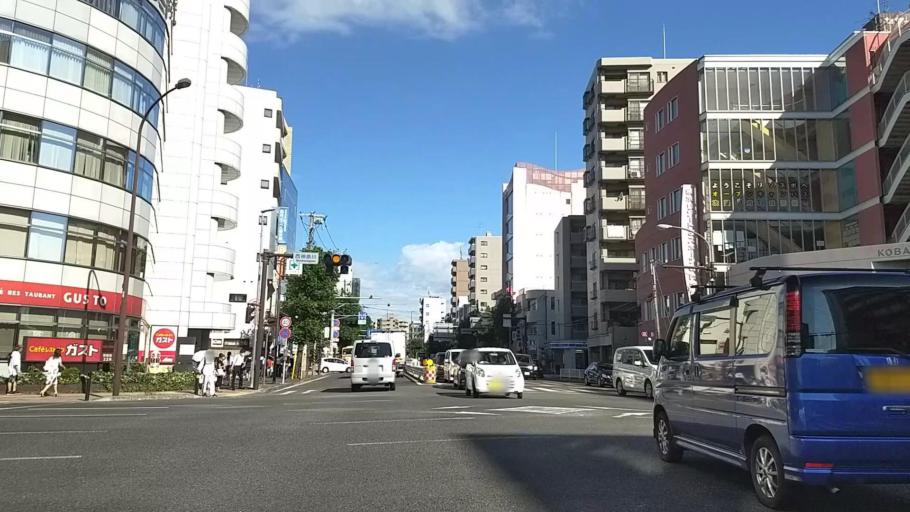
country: JP
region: Kanagawa
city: Yokohama
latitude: 35.4800
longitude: 139.6319
